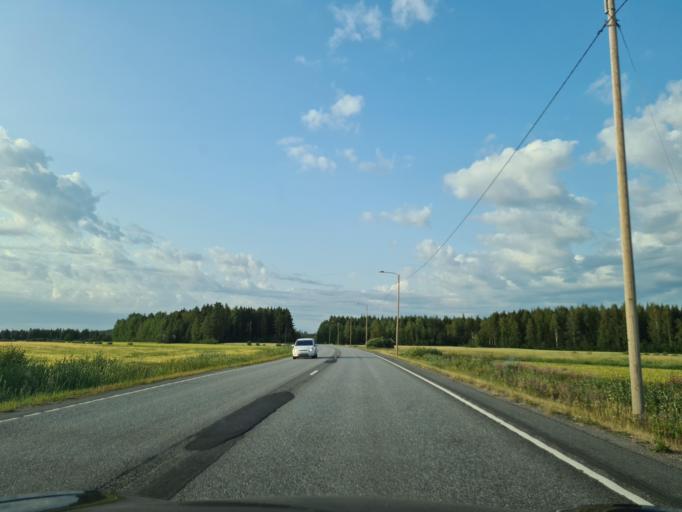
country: FI
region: Southern Ostrobothnia
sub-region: Seinaejoki
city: Kauhava
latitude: 63.0619
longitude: 23.0413
